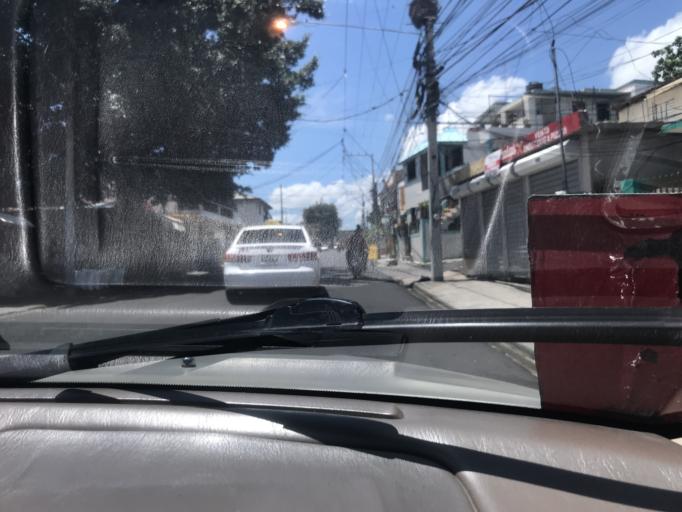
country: DO
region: Santiago
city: Santiago de los Caballeros
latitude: 19.4248
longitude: -70.6910
